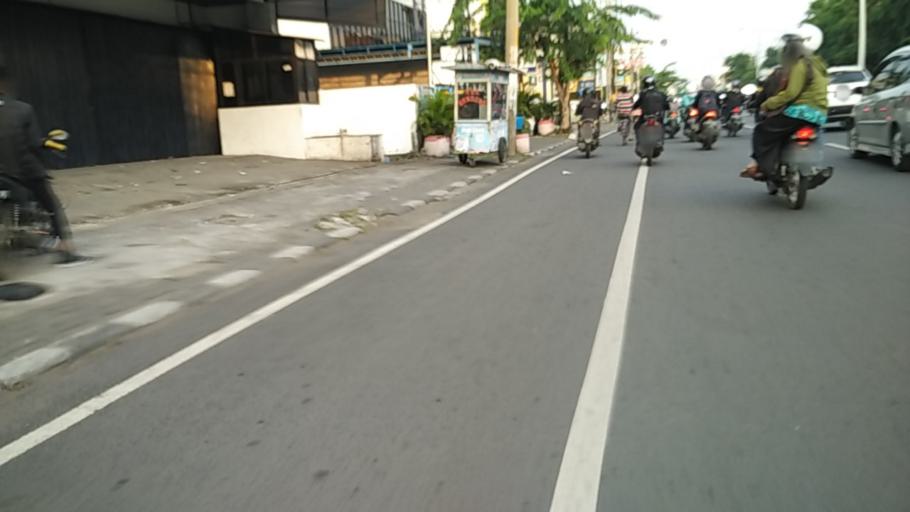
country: ID
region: Central Java
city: Semarang
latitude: -6.9983
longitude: 110.4416
